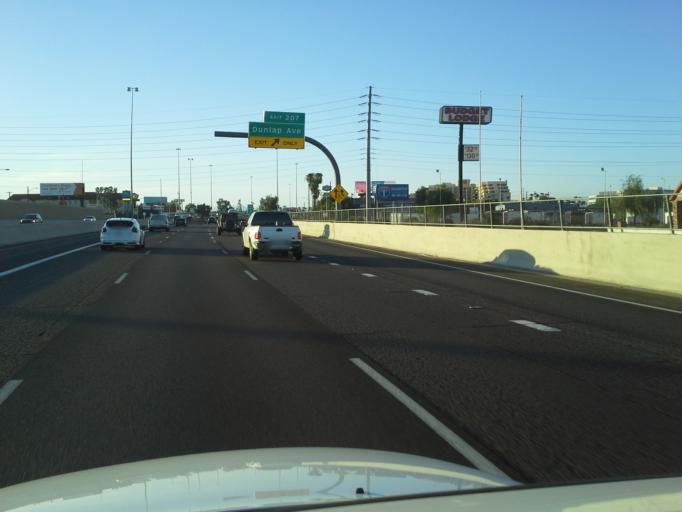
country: US
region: Arizona
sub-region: Maricopa County
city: Glendale
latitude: 33.5628
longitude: -112.1160
